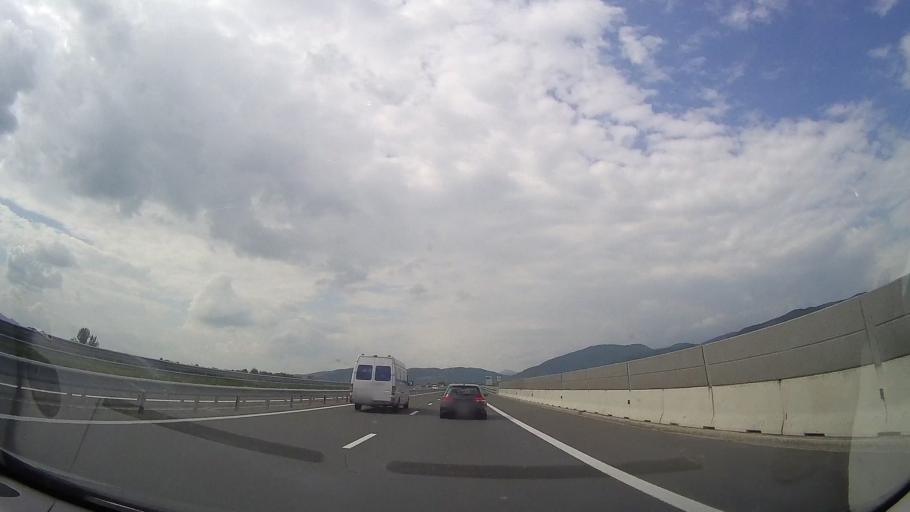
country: RO
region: Hunedoara
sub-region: Oras Simeria
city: Simeria
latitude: 45.8601
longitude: 23.0279
